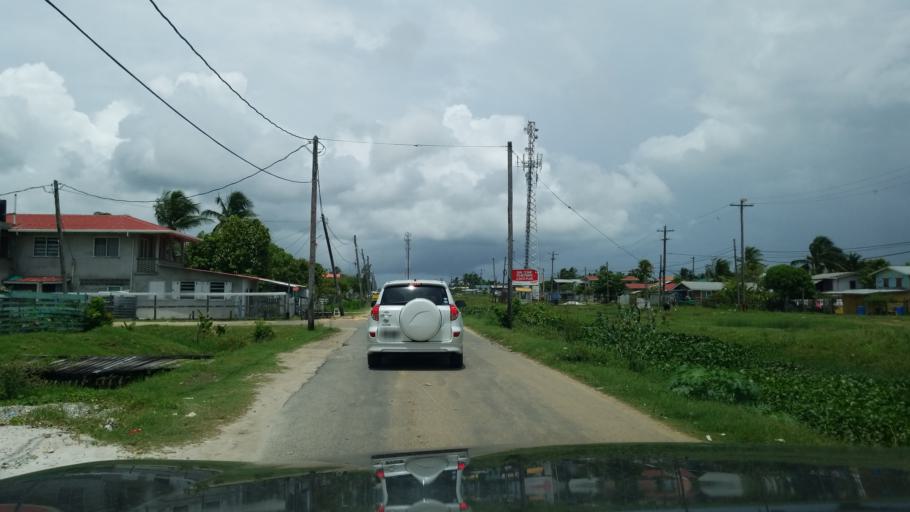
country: GY
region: Demerara-Mahaica
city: Georgetown
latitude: 6.8082
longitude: -58.1213
